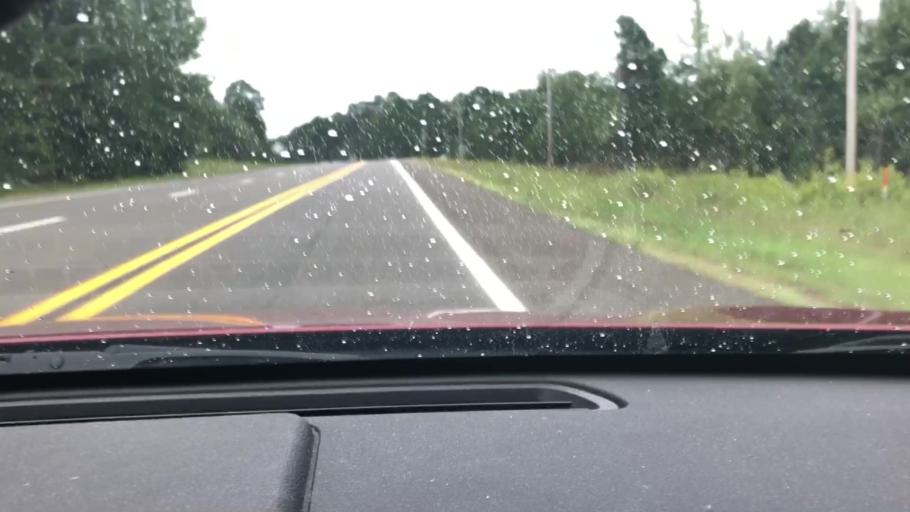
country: US
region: Arkansas
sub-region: Columbia County
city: Waldo
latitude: 33.3504
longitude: -93.3566
